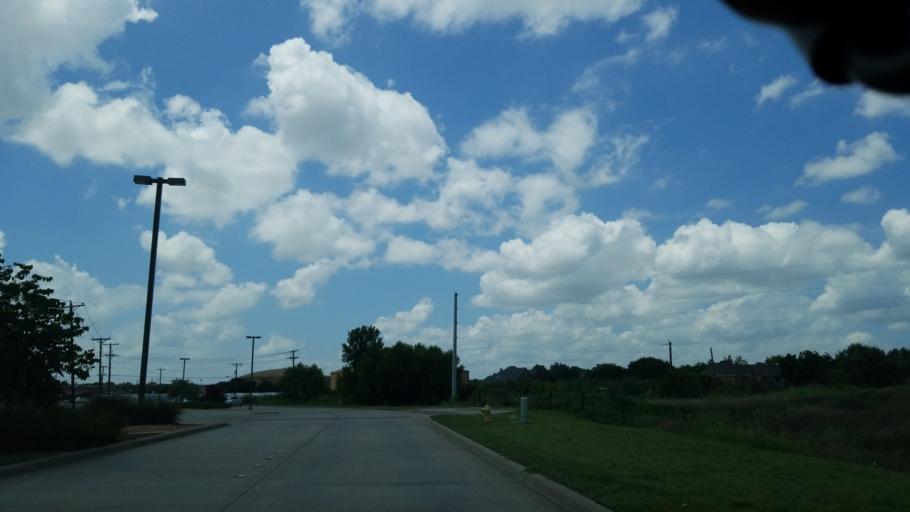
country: US
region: Texas
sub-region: Dallas County
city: Coppell
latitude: 32.9688
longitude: -96.9547
